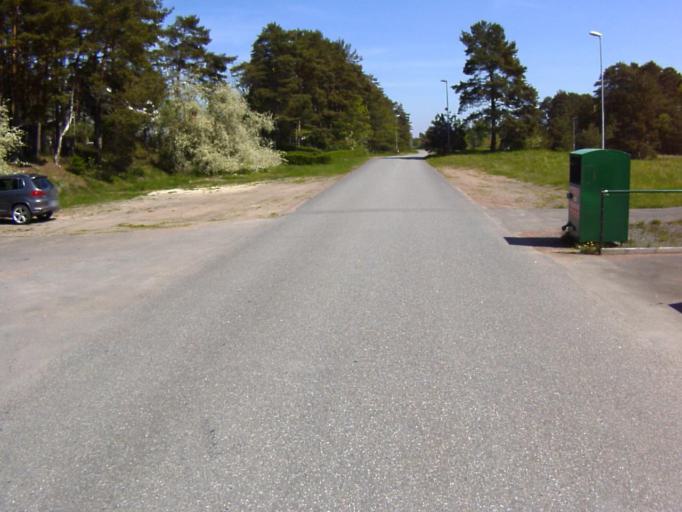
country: SE
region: Skane
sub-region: Kristianstads Kommun
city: Degeberga
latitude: 55.9003
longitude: 14.0859
